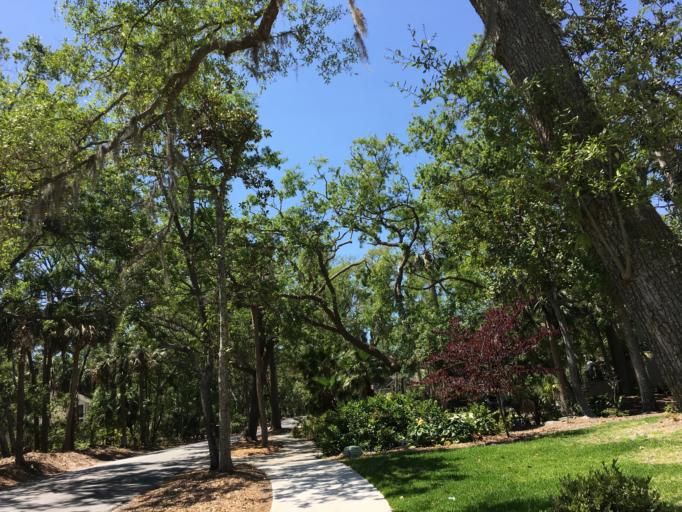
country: US
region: South Carolina
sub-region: Beaufort County
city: Hilton Head Island
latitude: 32.1814
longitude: -80.7077
